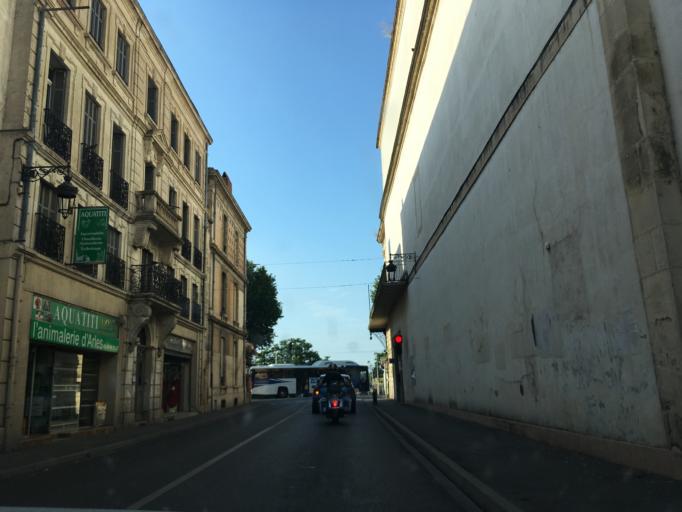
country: FR
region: Provence-Alpes-Cote d'Azur
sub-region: Departement des Bouches-du-Rhone
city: Arles
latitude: 43.6756
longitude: 4.6249
